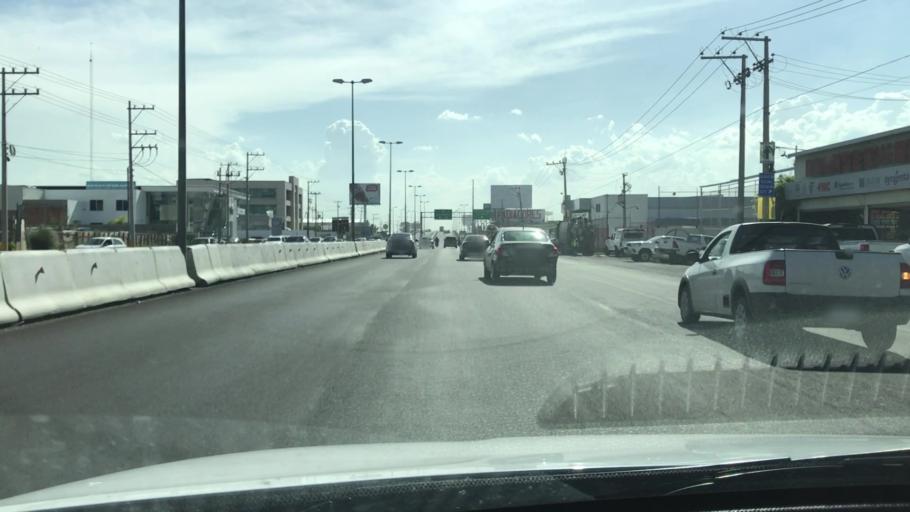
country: MX
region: Guanajuato
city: Celaya
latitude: 20.5191
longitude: -100.8431
